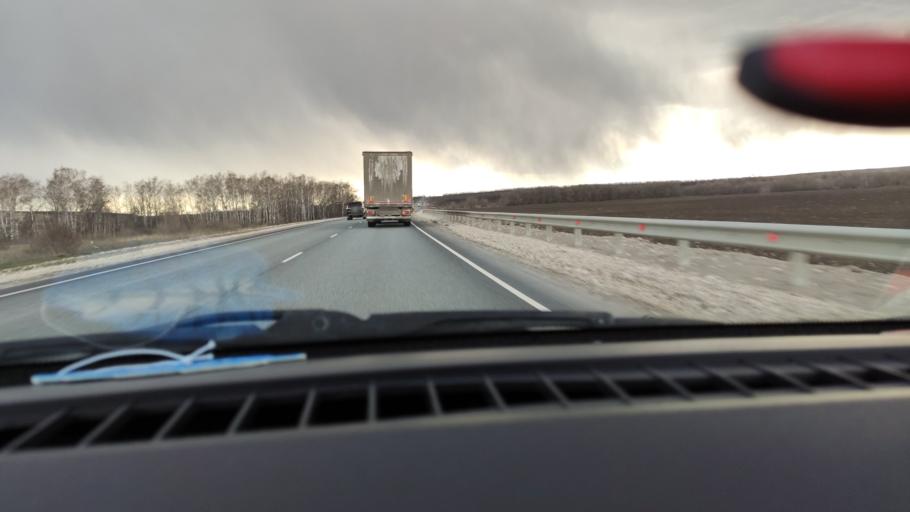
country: RU
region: Saratov
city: Yelshanka
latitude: 51.8529
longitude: 46.4911
